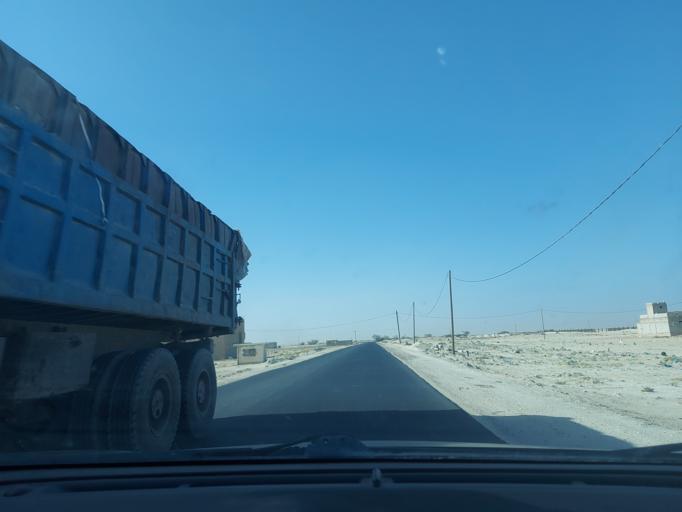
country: MR
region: Nouakchott
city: Nouakchott
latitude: 17.9956
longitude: -15.9882
